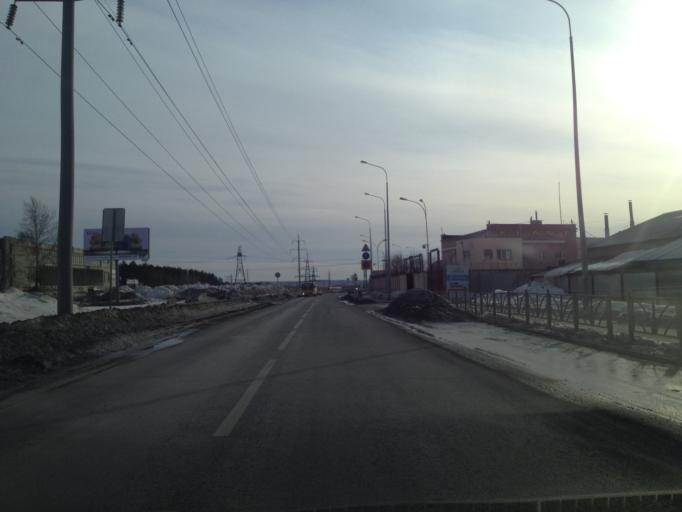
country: RU
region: Sverdlovsk
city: Sovkhoznyy
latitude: 56.7553
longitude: 60.5859
